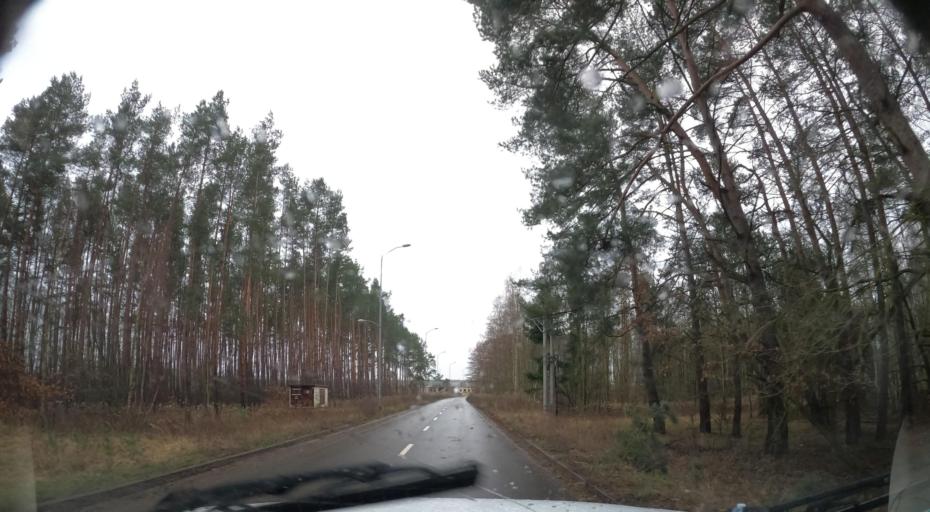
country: PL
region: West Pomeranian Voivodeship
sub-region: Powiat gryfinski
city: Stare Czarnowo
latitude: 53.3907
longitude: 14.7264
